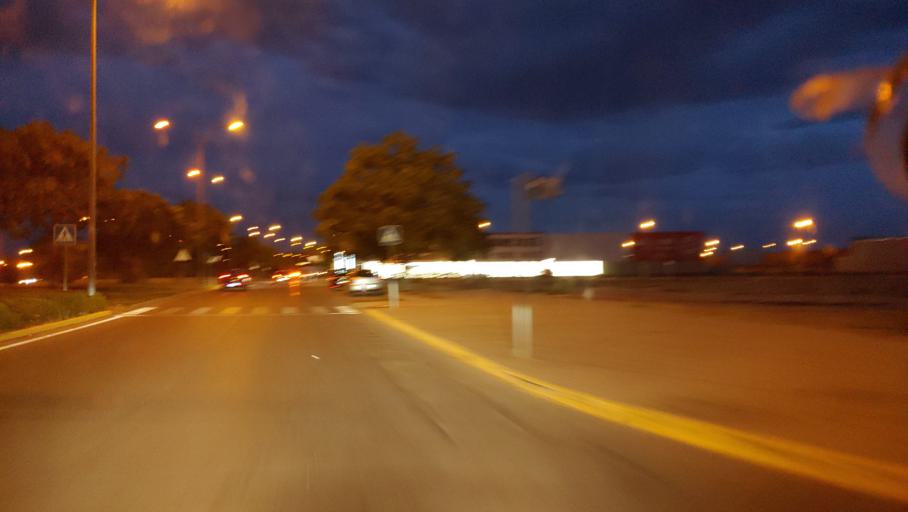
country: ES
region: Castille-La Mancha
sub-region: Provincia de Ciudad Real
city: Ciudad Real
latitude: 38.9849
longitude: -3.9111
